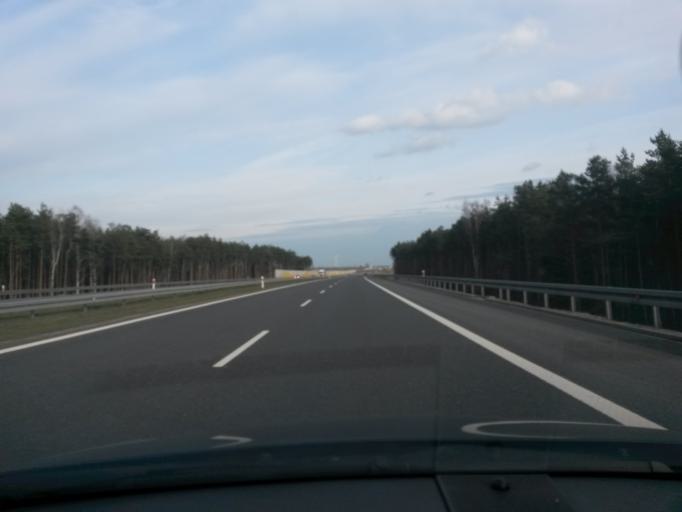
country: PL
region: Lodz Voivodeship
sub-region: Powiat leczycki
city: Swinice Warckie
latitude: 52.0257
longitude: 18.9165
